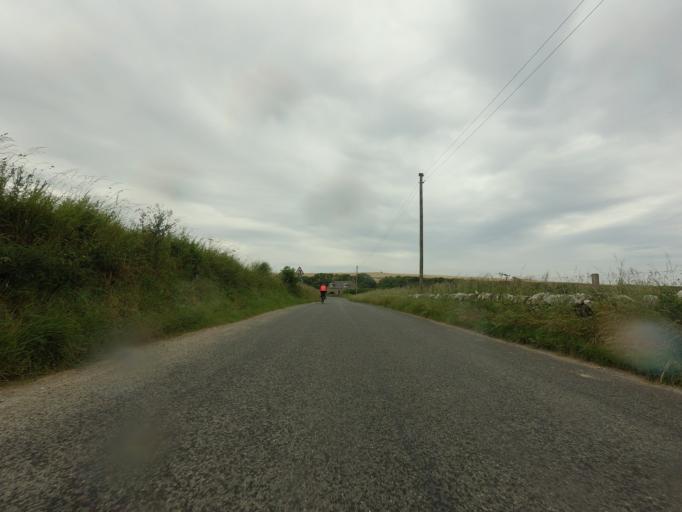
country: GB
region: Scotland
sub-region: Aberdeenshire
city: Portsoy
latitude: 57.6766
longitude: -2.6504
